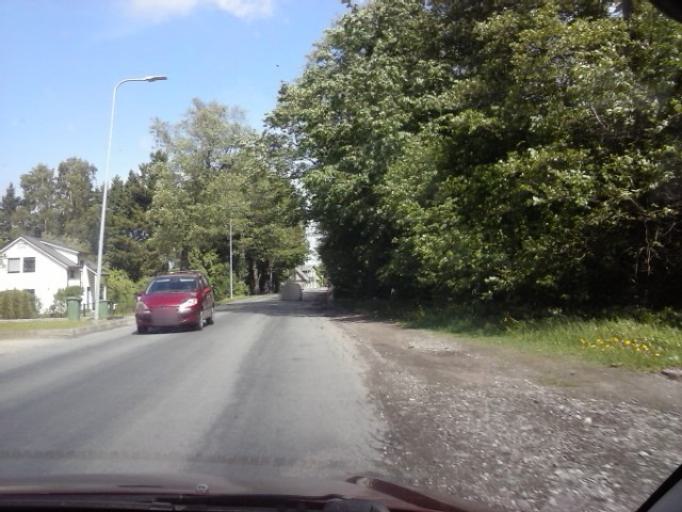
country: EE
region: Laeaene
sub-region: Haapsalu linn
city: Haapsalu
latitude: 58.9360
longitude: 23.5631
